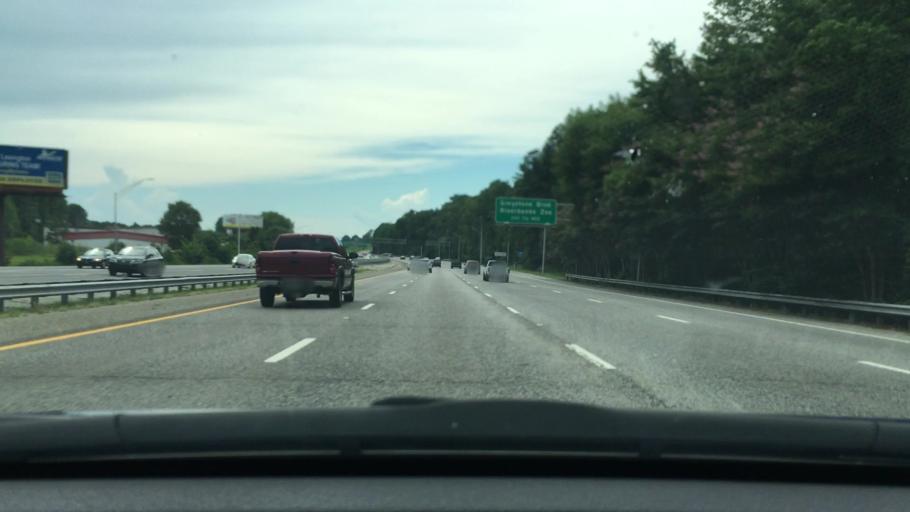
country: US
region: South Carolina
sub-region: Lexington County
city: West Columbia
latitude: 34.0111
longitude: -81.0662
